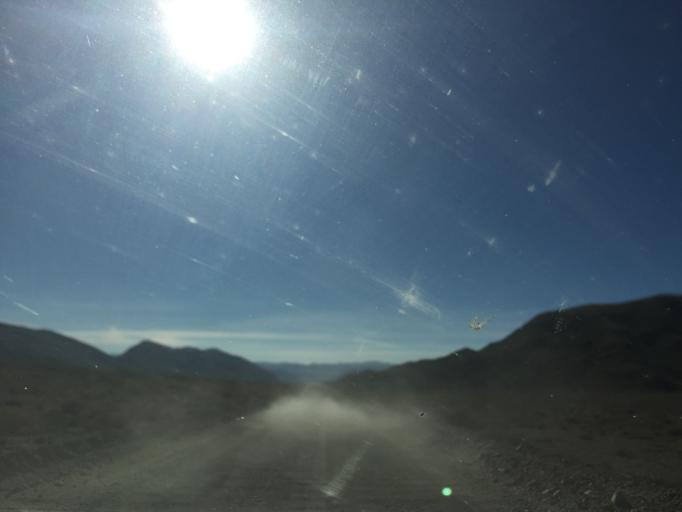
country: US
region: California
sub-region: Inyo County
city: Lone Pine
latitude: 36.8088
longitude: -117.5114
